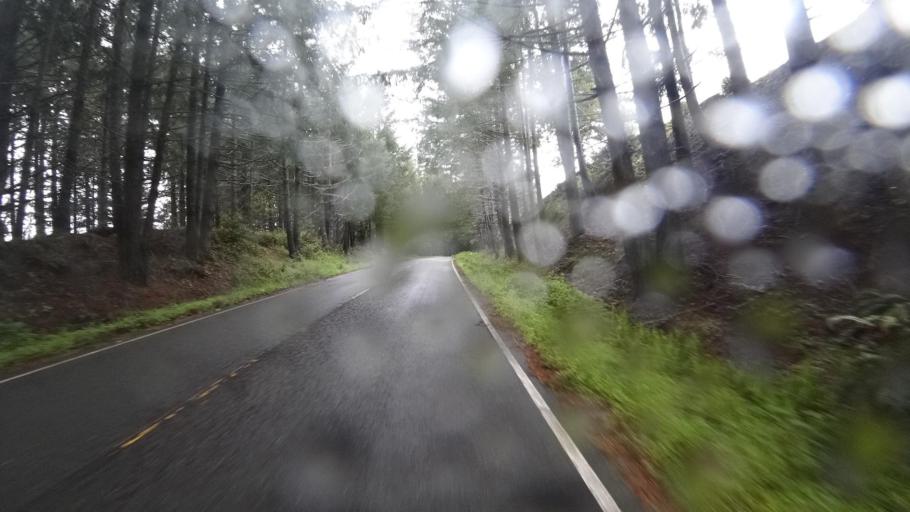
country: US
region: California
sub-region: Humboldt County
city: Westhaven-Moonstone
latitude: 41.1904
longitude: -123.9337
